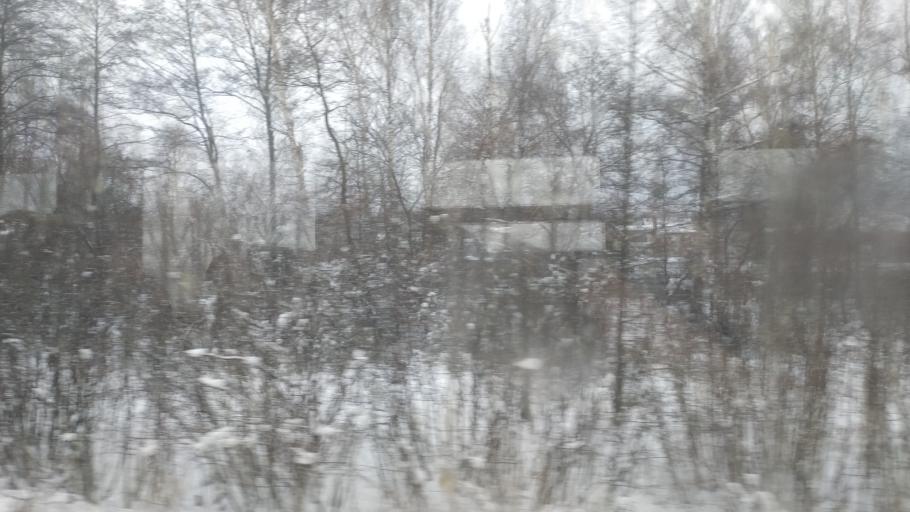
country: RU
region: Moskovskaya
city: Malyshevo
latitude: 55.5386
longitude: 38.2999
